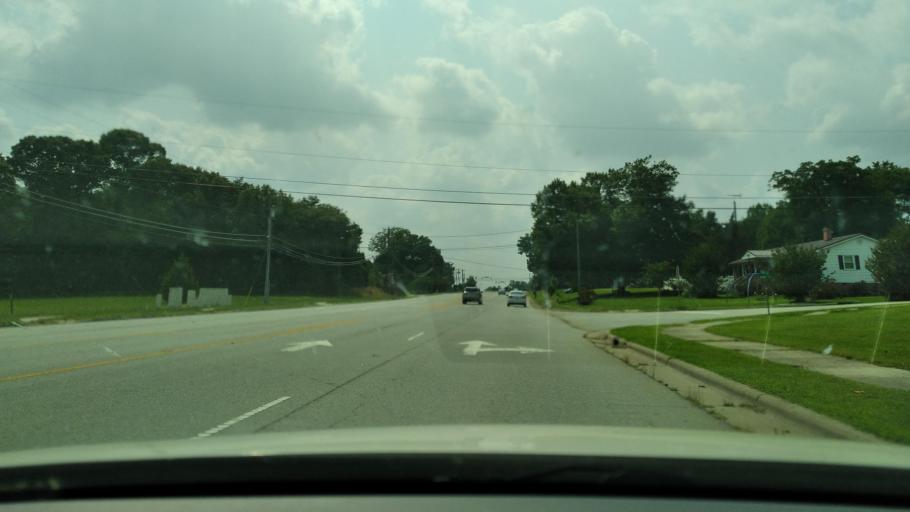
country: US
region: North Carolina
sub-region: Guilford County
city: Jamestown
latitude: 36.0391
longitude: -79.9153
